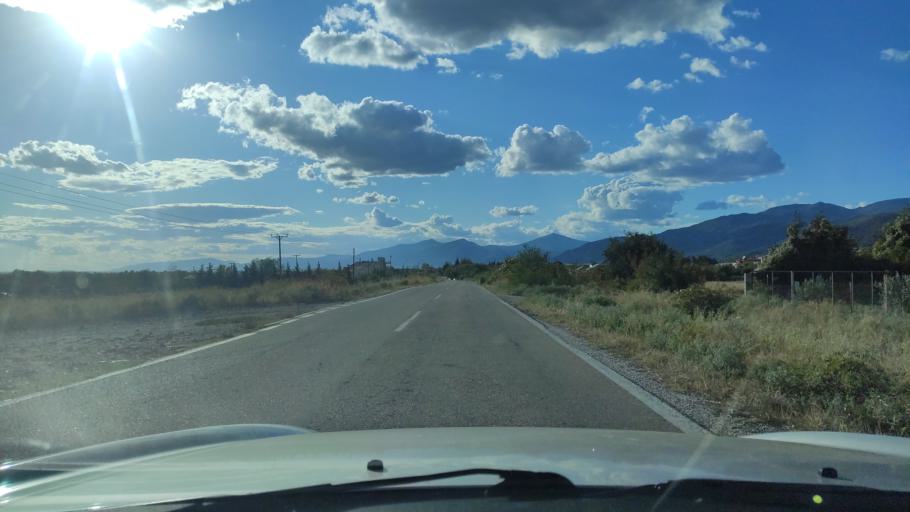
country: GR
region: East Macedonia and Thrace
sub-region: Nomos Xanthis
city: Selero
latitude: 41.1220
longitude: 25.0718
